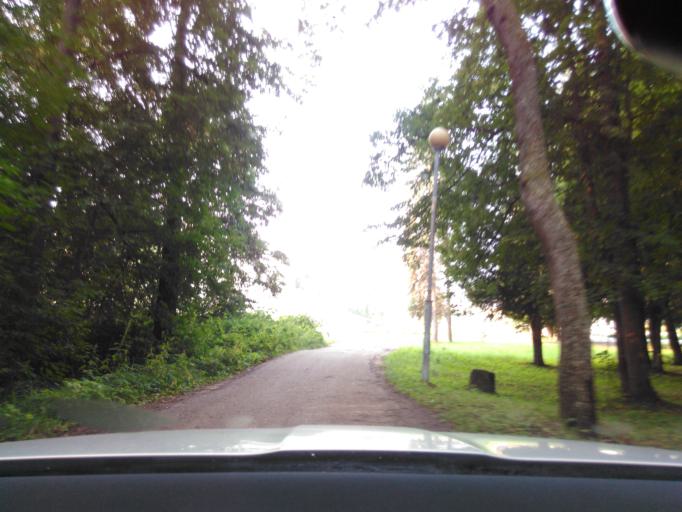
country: RU
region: Tverskaya
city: Konakovo
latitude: 56.6866
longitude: 36.6995
